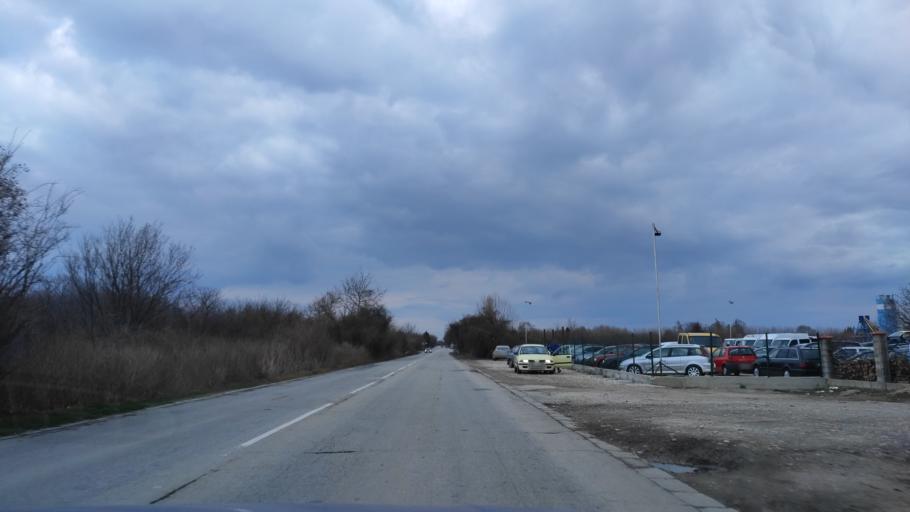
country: BG
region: Varna
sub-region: Obshtina Aksakovo
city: Aksakovo
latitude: 43.2295
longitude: 27.8201
